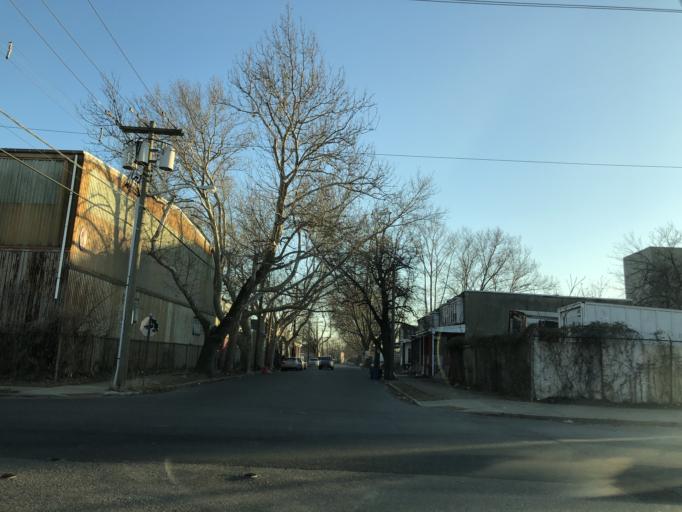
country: US
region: New Jersey
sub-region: Camden County
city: Camden
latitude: 39.9287
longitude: -75.1218
